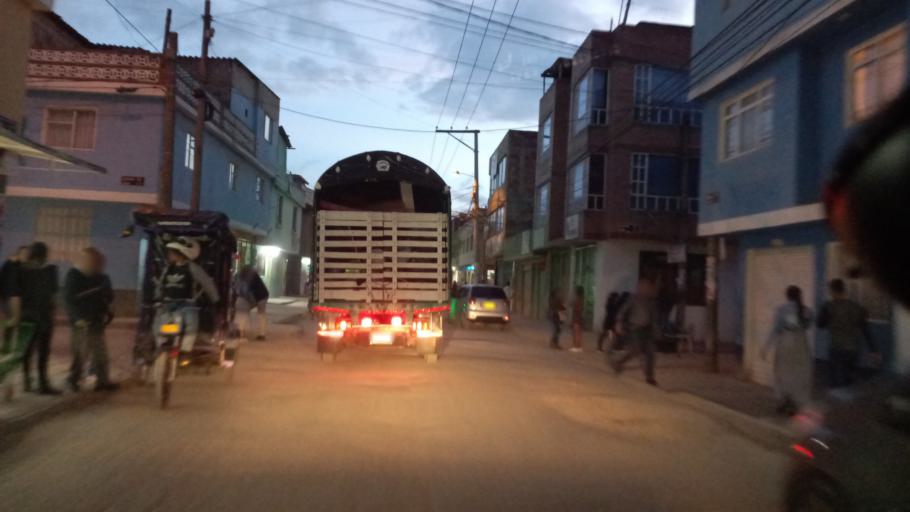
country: CO
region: Cundinamarca
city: Soacha
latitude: 4.5712
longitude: -74.2325
